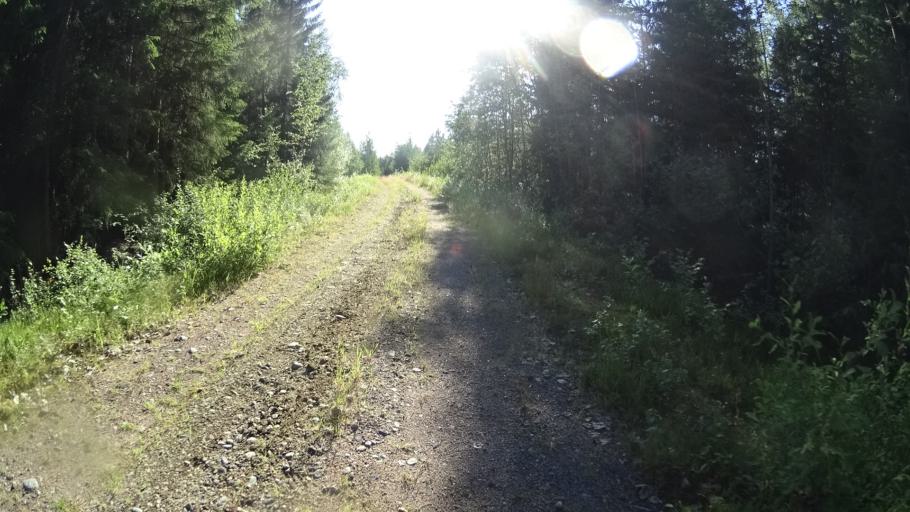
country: FI
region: Uusimaa
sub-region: Helsinki
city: Karkkila
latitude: 60.6555
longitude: 24.1370
